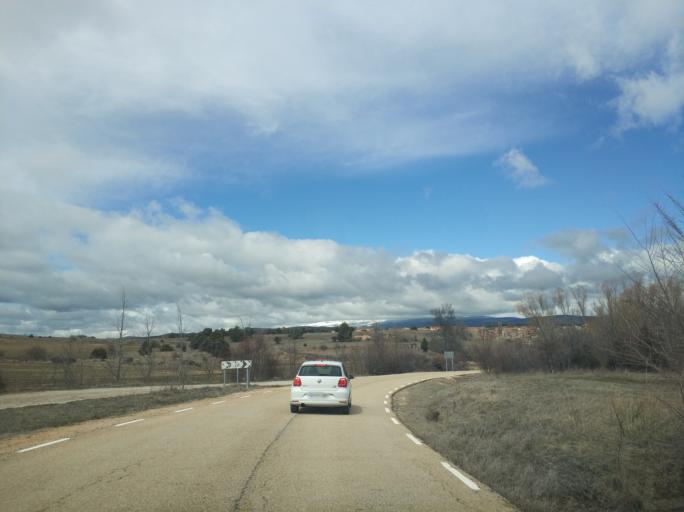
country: ES
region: Castille and Leon
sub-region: Provincia de Soria
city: Abejar
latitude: 41.7997
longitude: -2.7814
